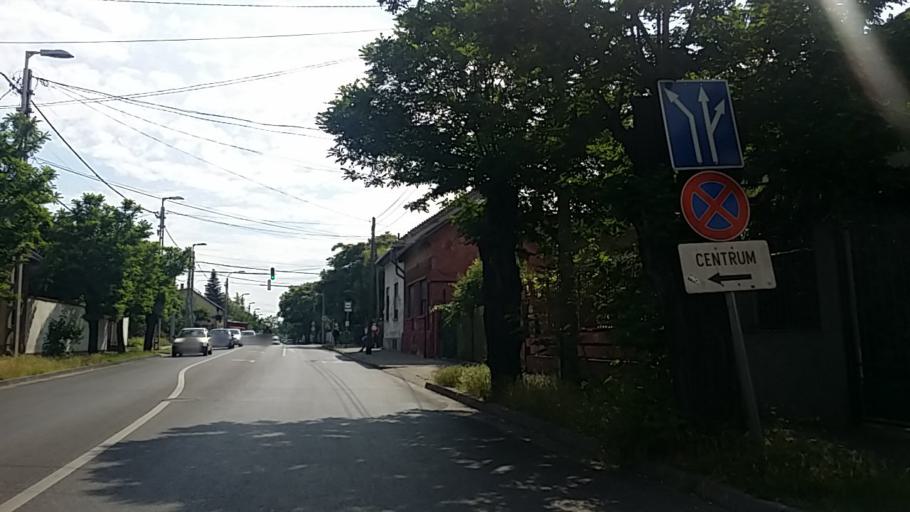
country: HU
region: Budapest
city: Budapest XIX. keruelet
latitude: 47.4497
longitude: 19.1319
